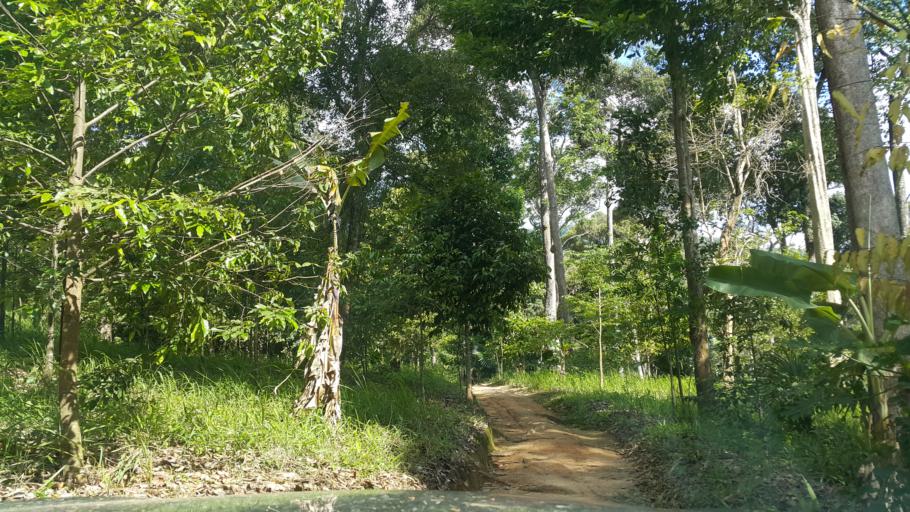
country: TH
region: Loei
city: Na Haeo
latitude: 17.5545
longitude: 100.9559
